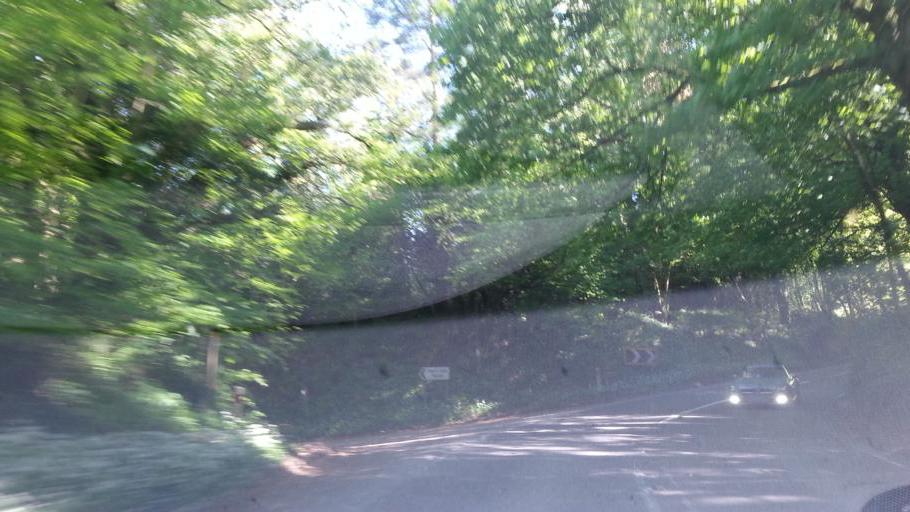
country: GB
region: England
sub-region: Dorset
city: Shaftesbury
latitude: 51.0310
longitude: -2.1892
